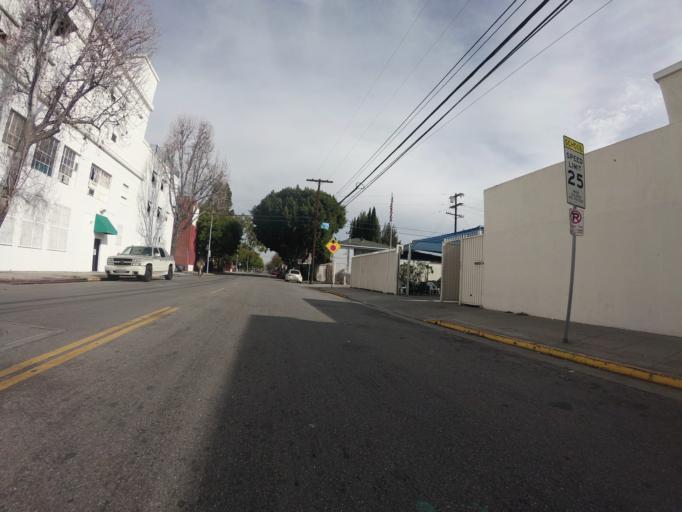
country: US
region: California
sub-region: Los Angeles County
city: Hollywood
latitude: 34.0871
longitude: -118.3383
